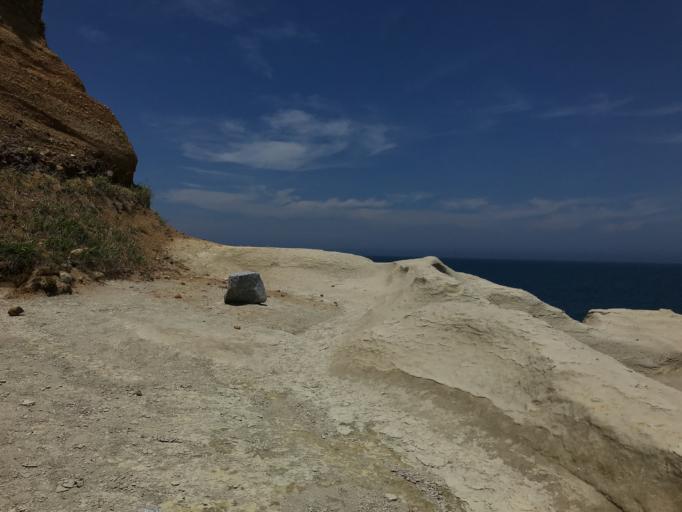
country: JP
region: Fukushima
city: Namie
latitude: 37.7626
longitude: 141.0004
